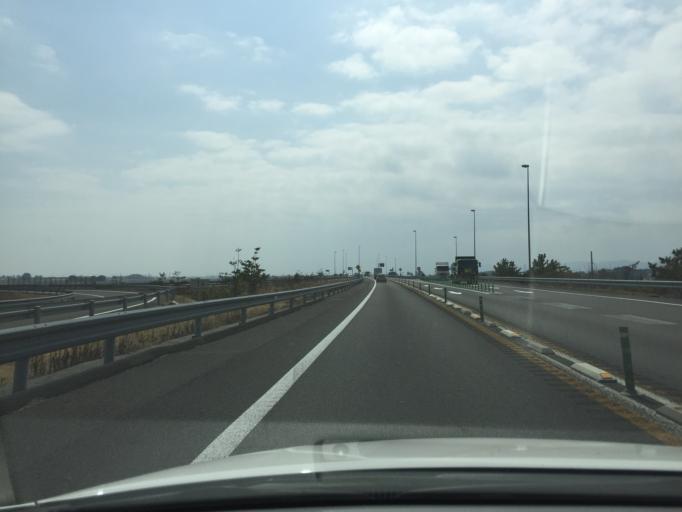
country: JP
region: Miyagi
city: Iwanuma
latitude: 38.0884
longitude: 140.8869
